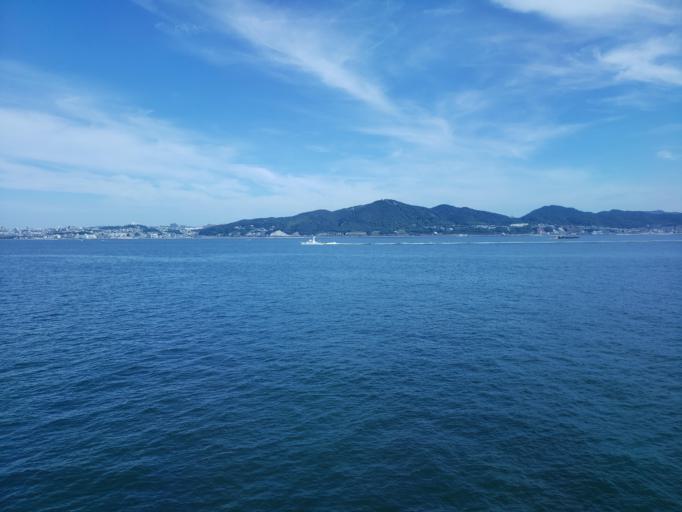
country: JP
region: Hyogo
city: Kobe
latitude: 34.6094
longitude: 135.1059
